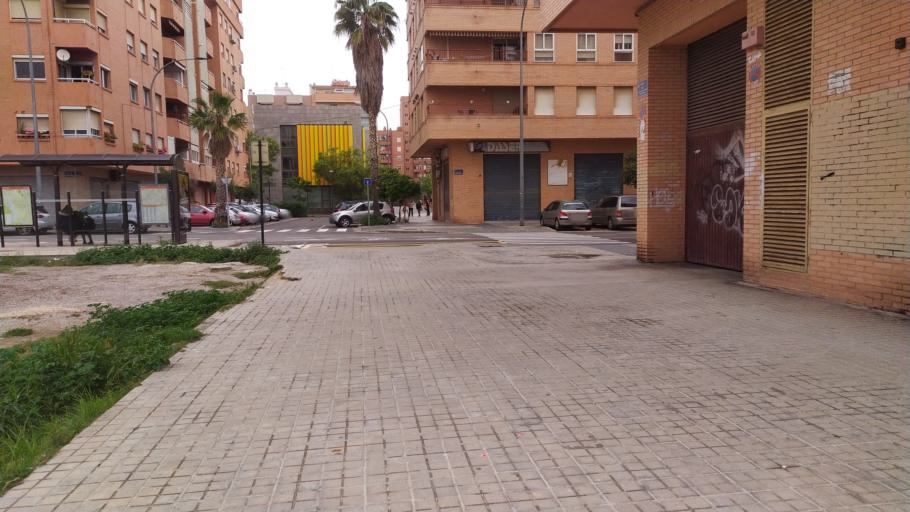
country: ES
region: Valencia
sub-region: Provincia de Valencia
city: Mislata
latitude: 39.4668
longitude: -0.4125
